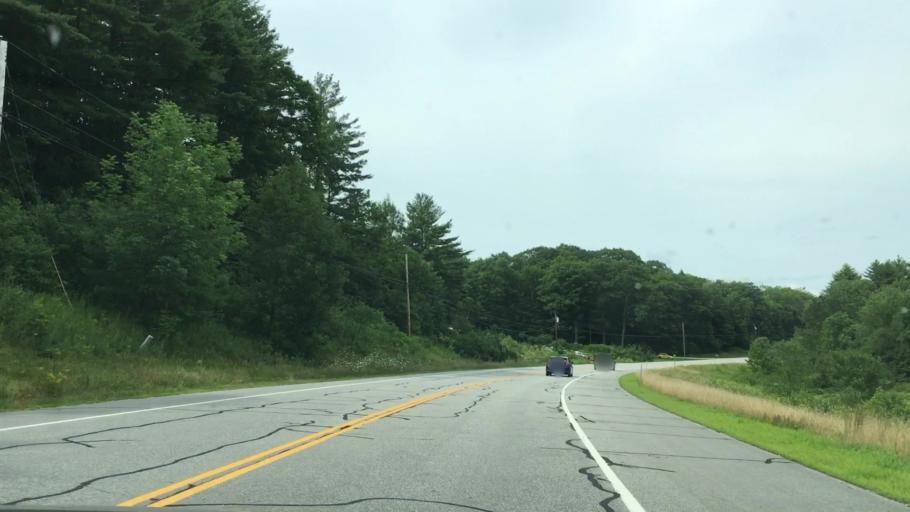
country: US
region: New Hampshire
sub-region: Hillsborough County
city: Hillsborough
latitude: 43.0946
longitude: -71.9207
